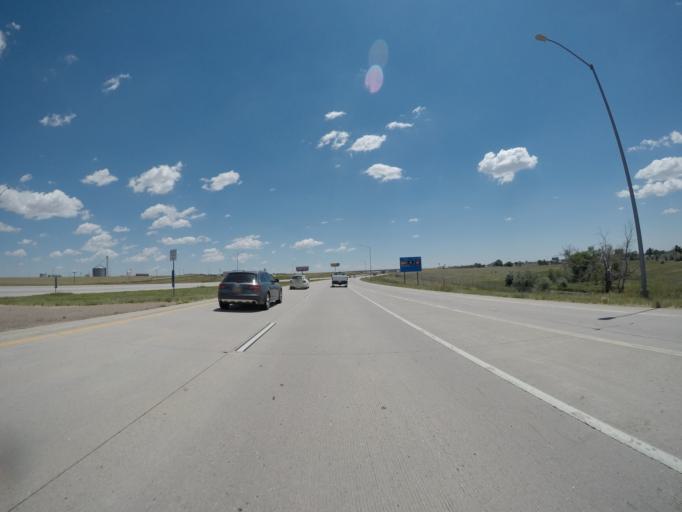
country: US
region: Colorado
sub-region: Lincoln County
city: Limon
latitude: 39.2728
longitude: -103.6833
